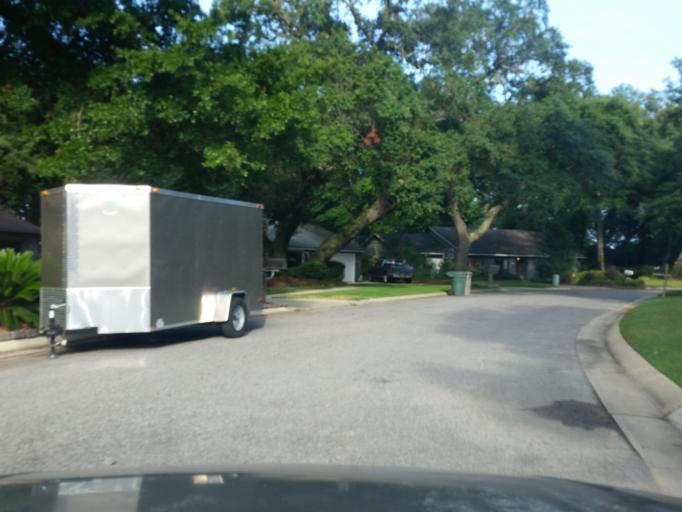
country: US
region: Florida
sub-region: Escambia County
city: Ferry Pass
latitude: 30.5019
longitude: -87.1633
